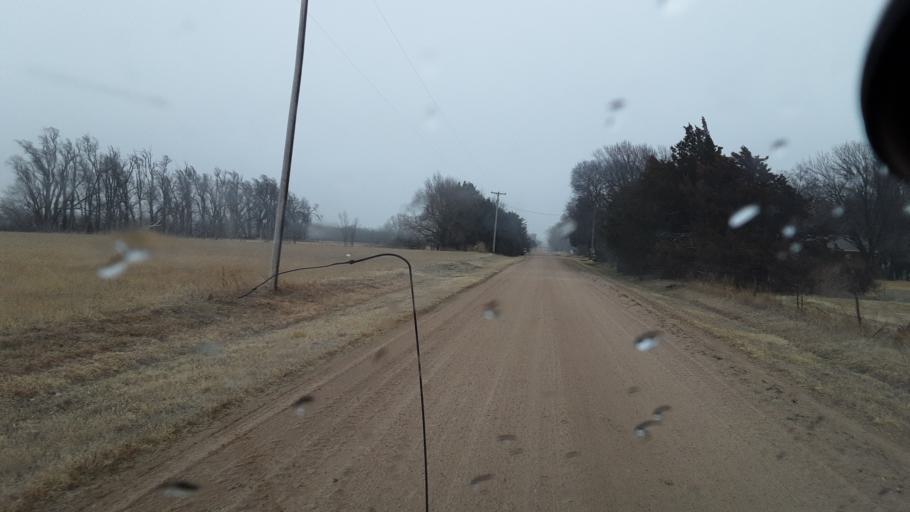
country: US
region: Kansas
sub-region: Reno County
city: South Hutchinson
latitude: 37.9555
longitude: -98.0289
